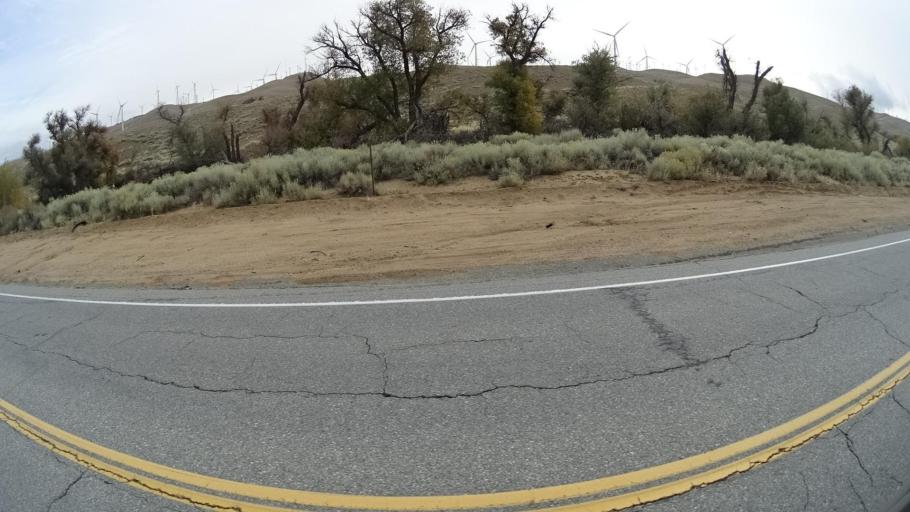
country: US
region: California
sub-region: Kern County
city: Tehachapi
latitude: 35.0772
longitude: -118.3966
